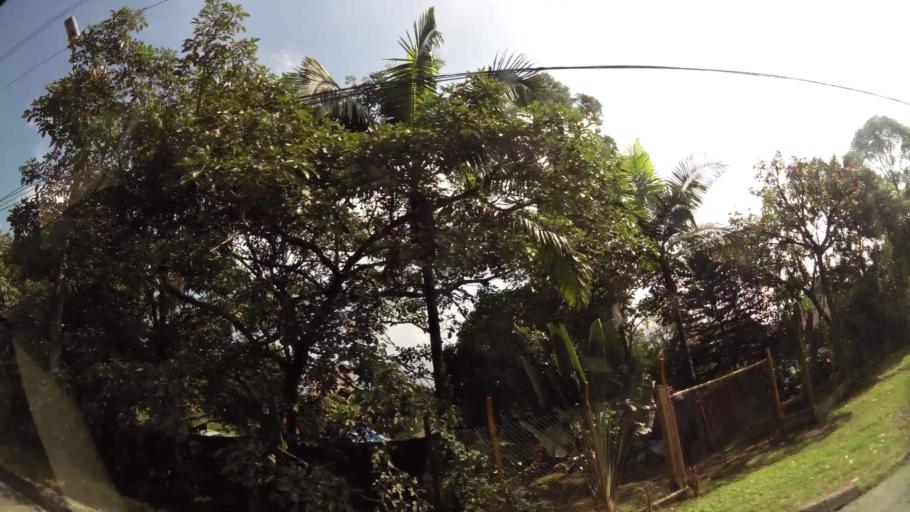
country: CO
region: Antioquia
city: La Estrella
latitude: 6.1687
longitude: -75.6389
